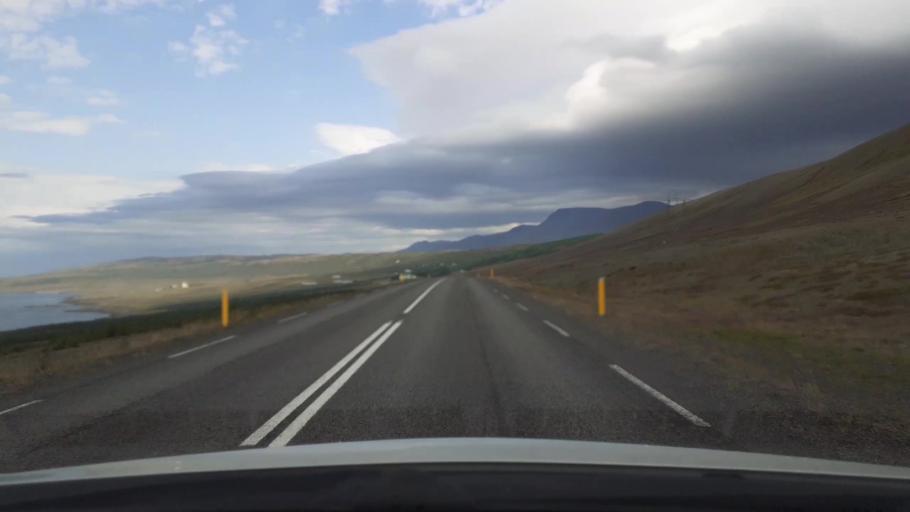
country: IS
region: Capital Region
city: Mosfellsbaer
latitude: 64.4038
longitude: -21.5655
